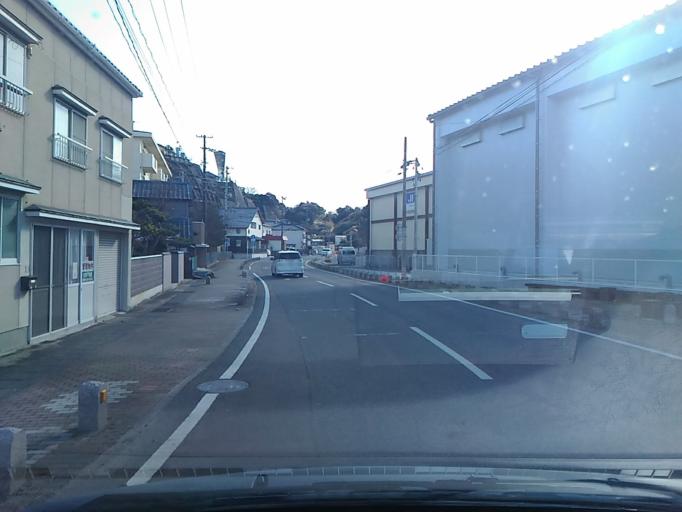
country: JP
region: Fukushima
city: Iwaki
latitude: 36.9431
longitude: 140.9148
